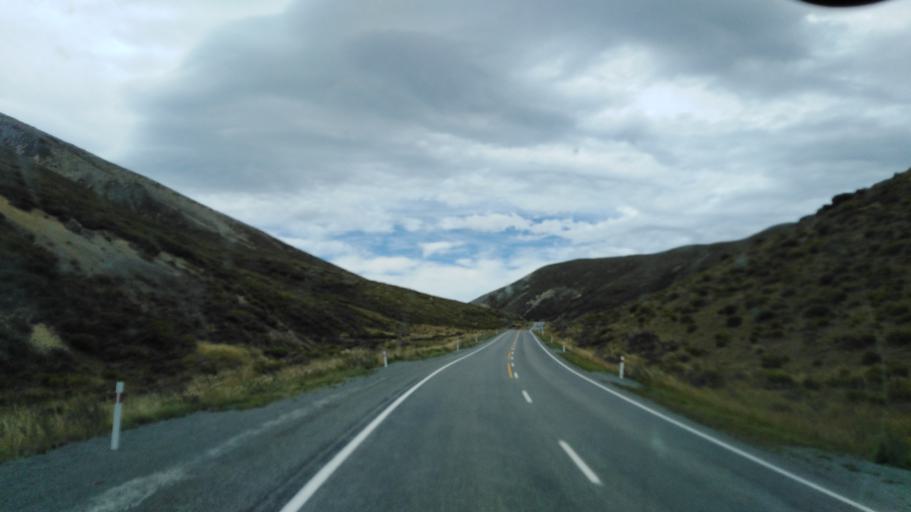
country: NZ
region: Canterbury
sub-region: Ashburton District
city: Methven
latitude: -43.2932
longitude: 171.7223
